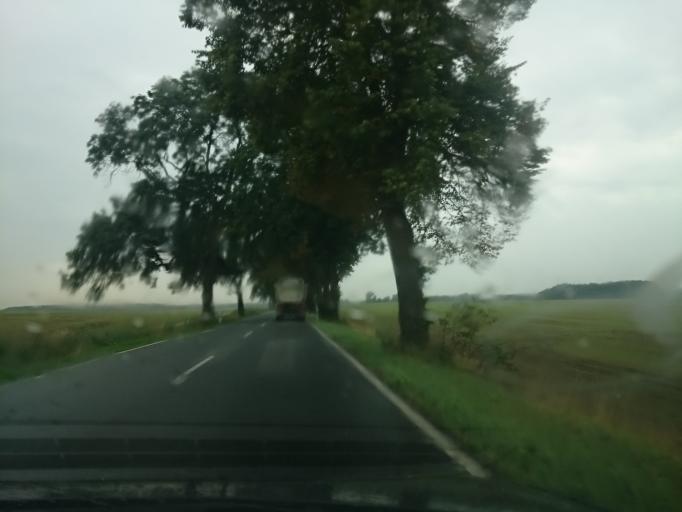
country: DE
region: Brandenburg
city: Gransee
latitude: 52.8912
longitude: 13.1548
